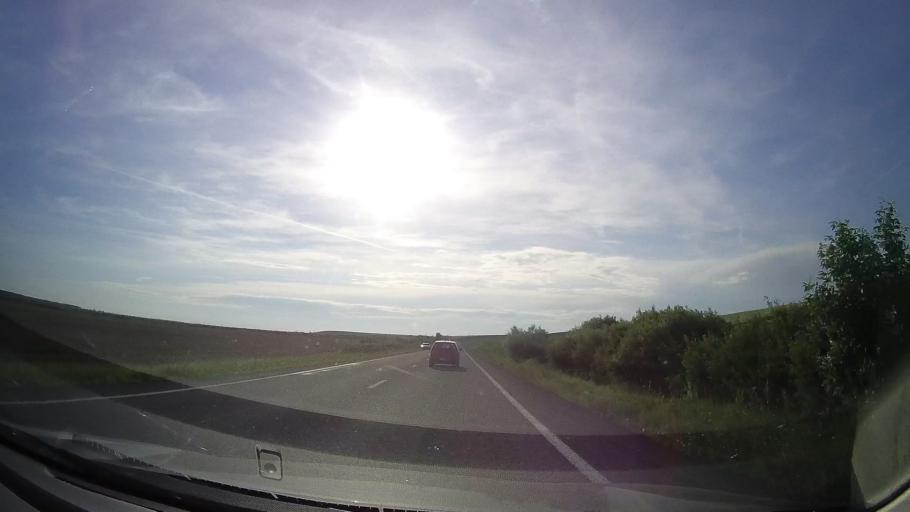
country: RO
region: Timis
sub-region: Oras Recas
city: Recas
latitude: 45.7930
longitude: 21.5591
